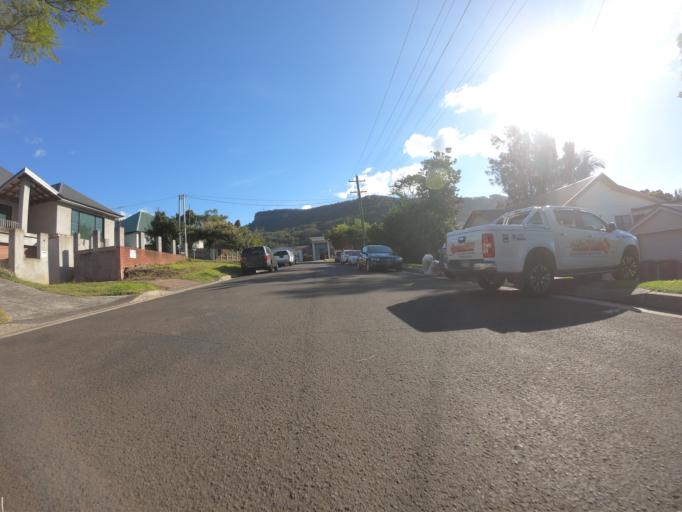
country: AU
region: New South Wales
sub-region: Wollongong
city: Corrimal
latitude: -34.3670
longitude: 150.8952
